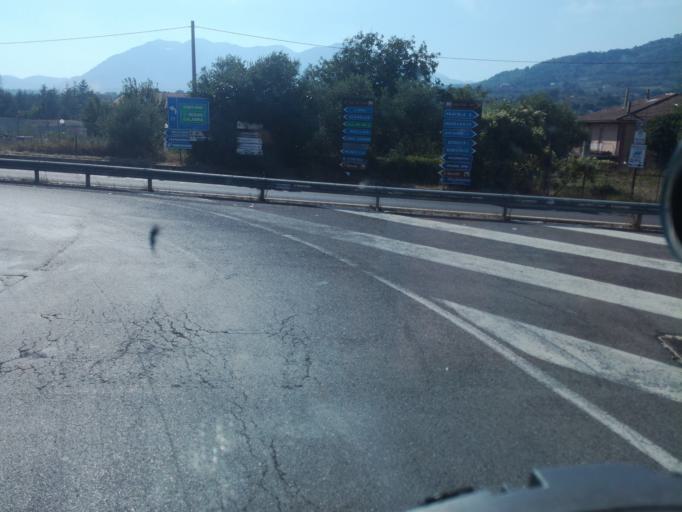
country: IT
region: Campania
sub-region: Provincia di Avellino
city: Manocalzati
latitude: 40.9473
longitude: 14.8342
